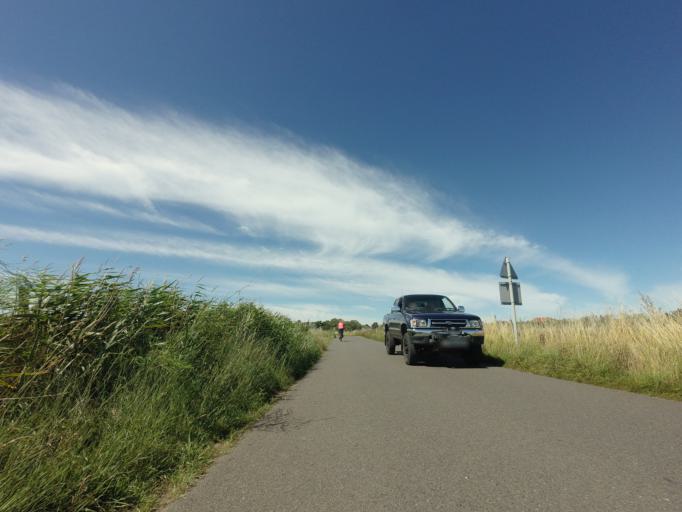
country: GB
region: England
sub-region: Kent
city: Deal
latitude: 51.2631
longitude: 1.3859
